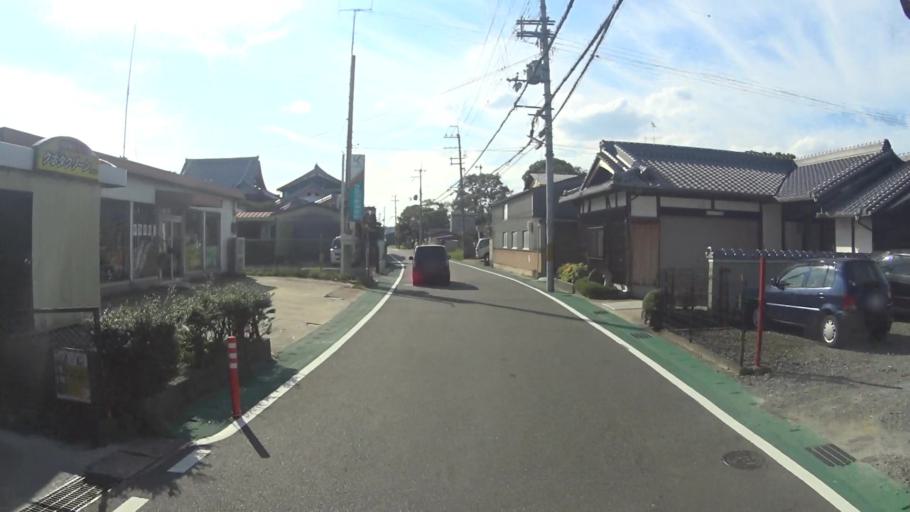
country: JP
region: Kyoto
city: Yawata
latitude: 34.8661
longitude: 135.7191
